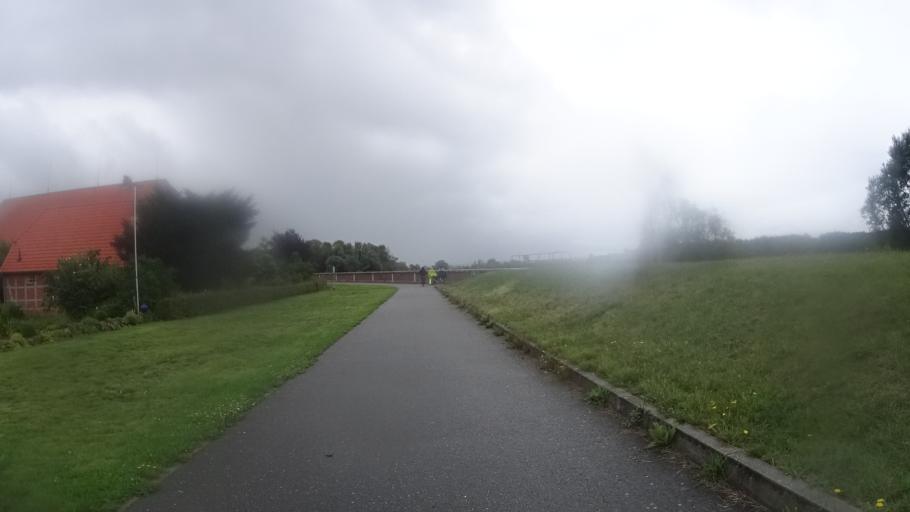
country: DE
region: Lower Saxony
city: Bleckede
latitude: 53.2858
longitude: 10.8042
